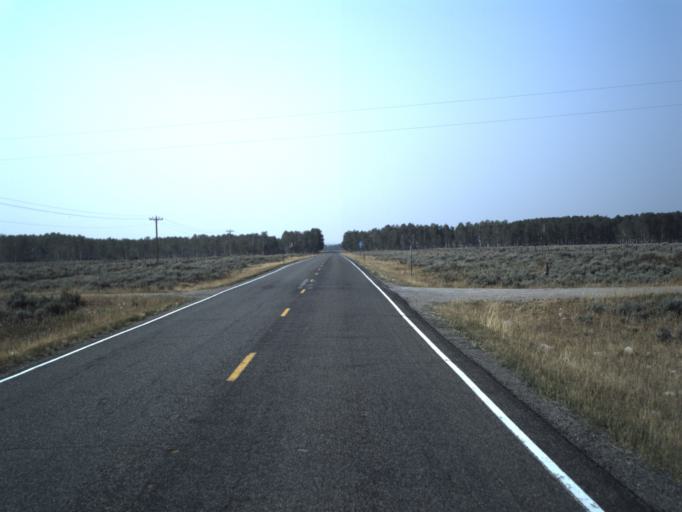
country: US
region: Wyoming
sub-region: Uinta County
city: Evanston
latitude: 40.9598
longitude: -110.8445
